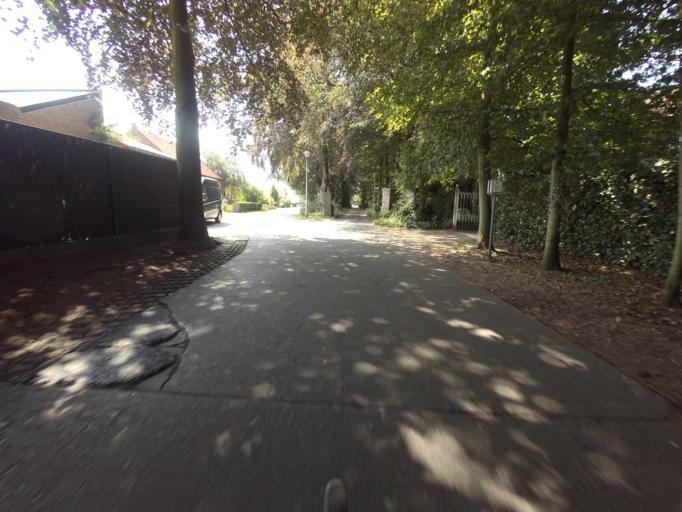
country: BE
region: Flanders
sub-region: Provincie West-Vlaanderen
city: Gistel
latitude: 51.1558
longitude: 2.9746
